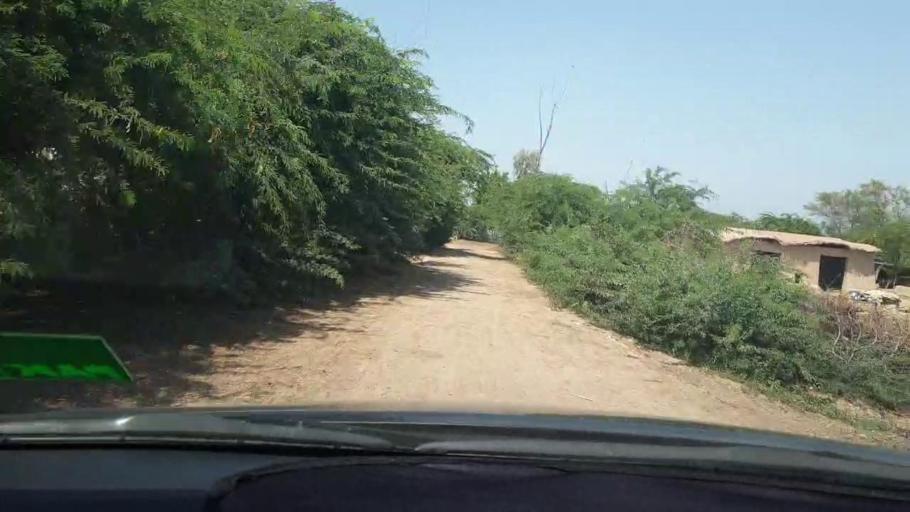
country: PK
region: Sindh
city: Digri
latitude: 24.9447
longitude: 69.1481
